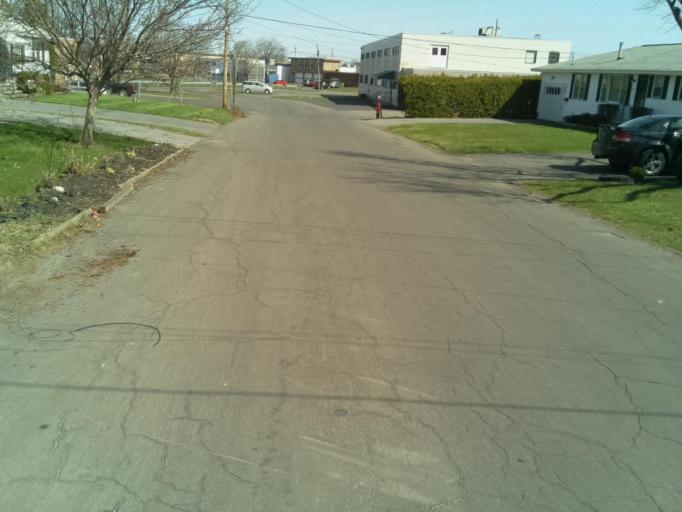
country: US
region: New York
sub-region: Onondaga County
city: Lyncourt
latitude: 43.0757
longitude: -76.1078
